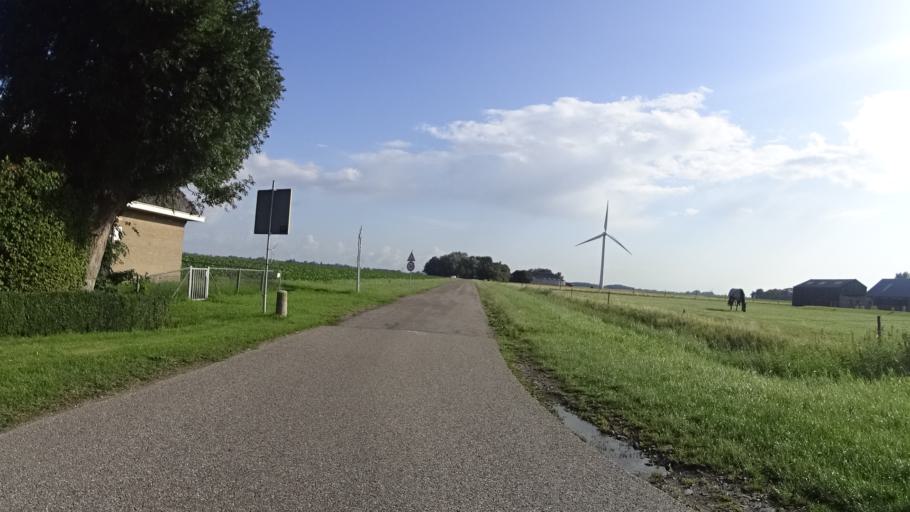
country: NL
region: Friesland
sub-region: Gemeente Harlingen
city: Harlingen
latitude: 53.1199
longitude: 5.4296
